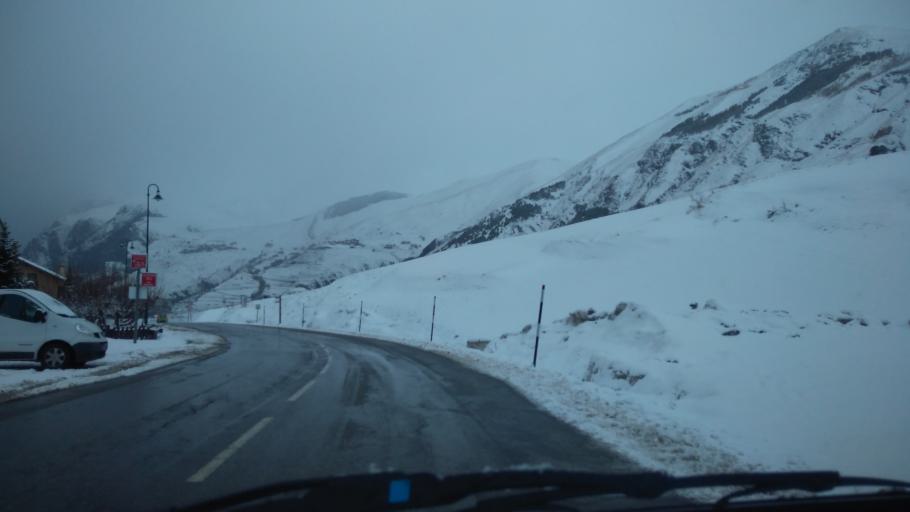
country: FR
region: Rhone-Alpes
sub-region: Departement de la Savoie
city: Valloire
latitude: 45.0442
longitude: 6.3370
